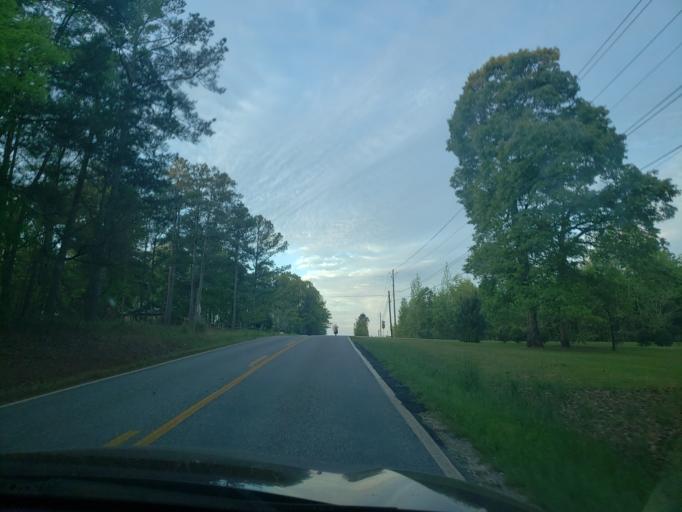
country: US
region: Alabama
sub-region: Elmore County
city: Tallassee
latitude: 32.6928
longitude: -85.8578
